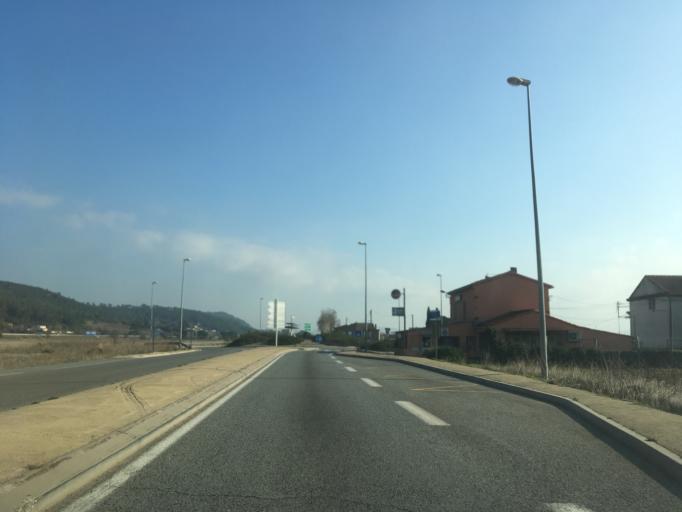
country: FR
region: Provence-Alpes-Cote d'Azur
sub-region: Departement du Var
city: Le Cannet-des-Maures
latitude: 43.3985
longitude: 6.3640
